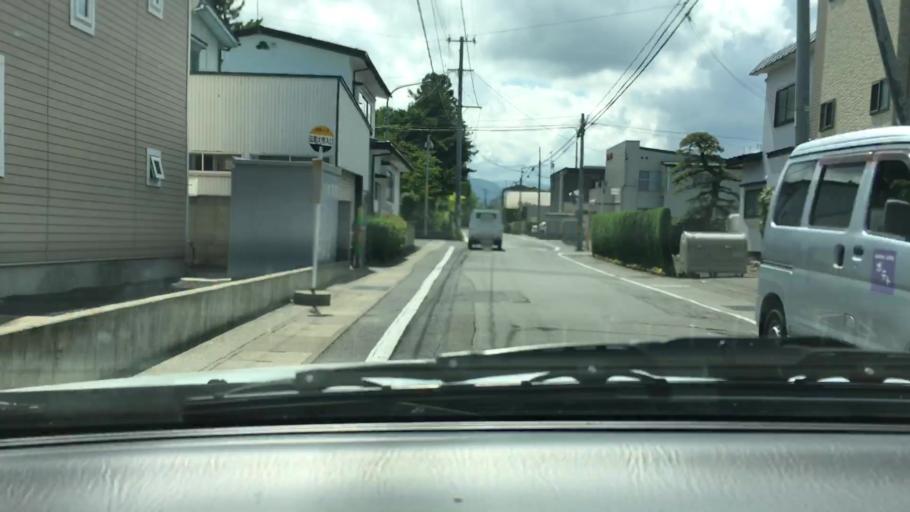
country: JP
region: Aomori
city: Hirosaki
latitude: 40.5909
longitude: 140.4710
